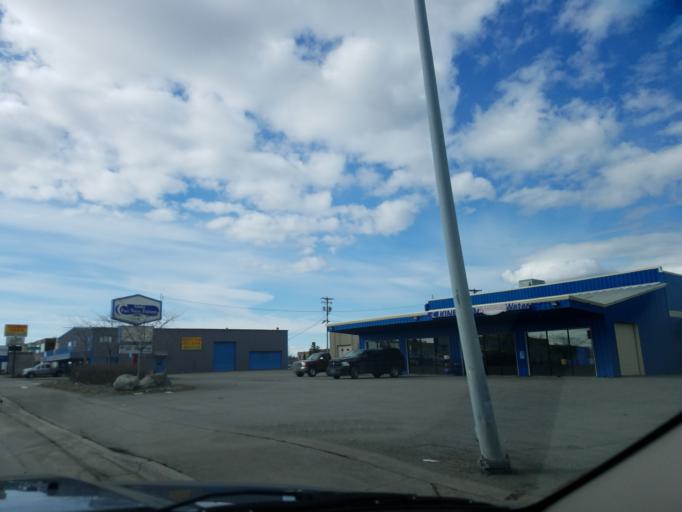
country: US
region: Alaska
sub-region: Anchorage Municipality
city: Anchorage
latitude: 61.1737
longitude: -149.8780
